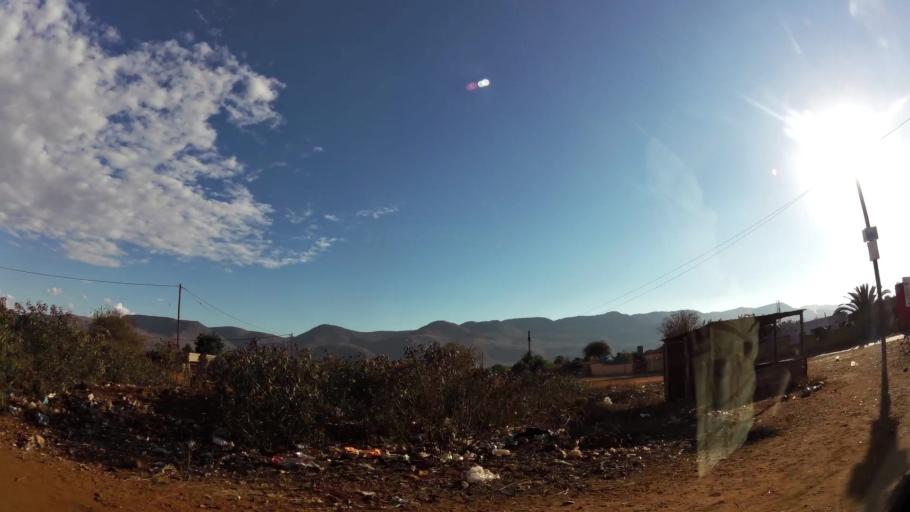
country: ZA
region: Limpopo
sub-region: Waterberg District Municipality
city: Mokopane
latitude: -24.1768
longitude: 28.9822
